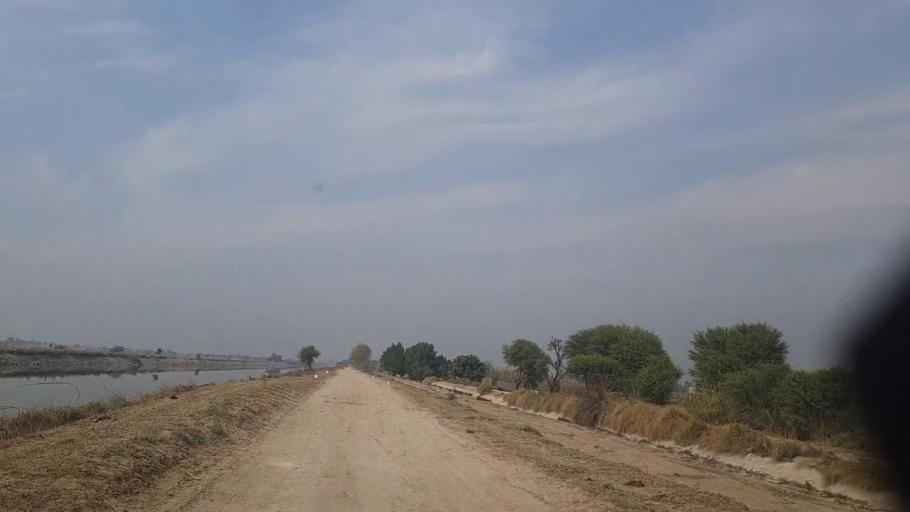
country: PK
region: Sindh
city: Daur
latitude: 26.3282
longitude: 68.1922
